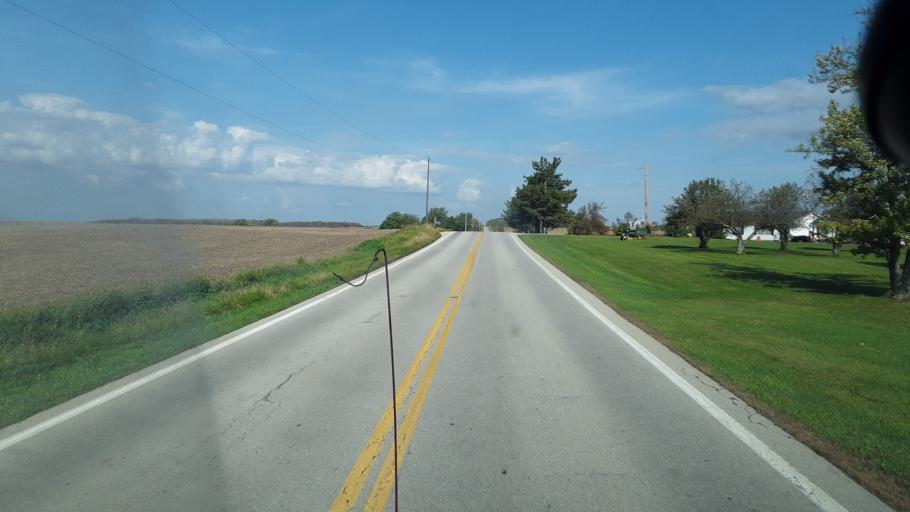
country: US
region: Ohio
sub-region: Clinton County
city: Sabina
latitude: 39.5200
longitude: -83.6949
